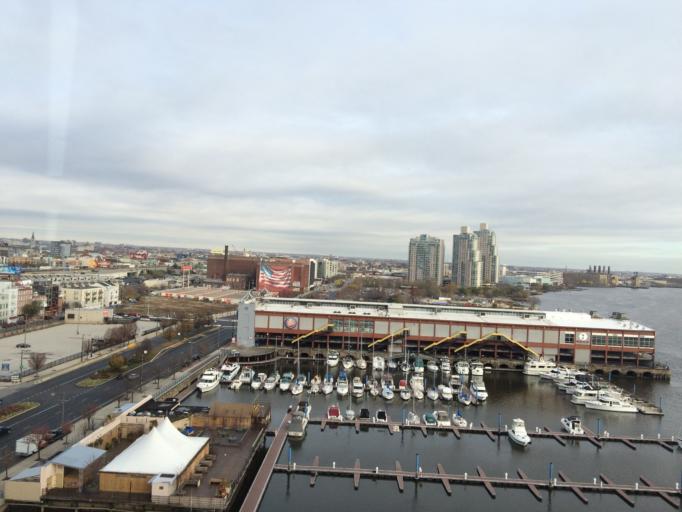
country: US
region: Pennsylvania
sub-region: Philadelphia County
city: Philadelphia
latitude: 39.9538
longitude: -75.1383
